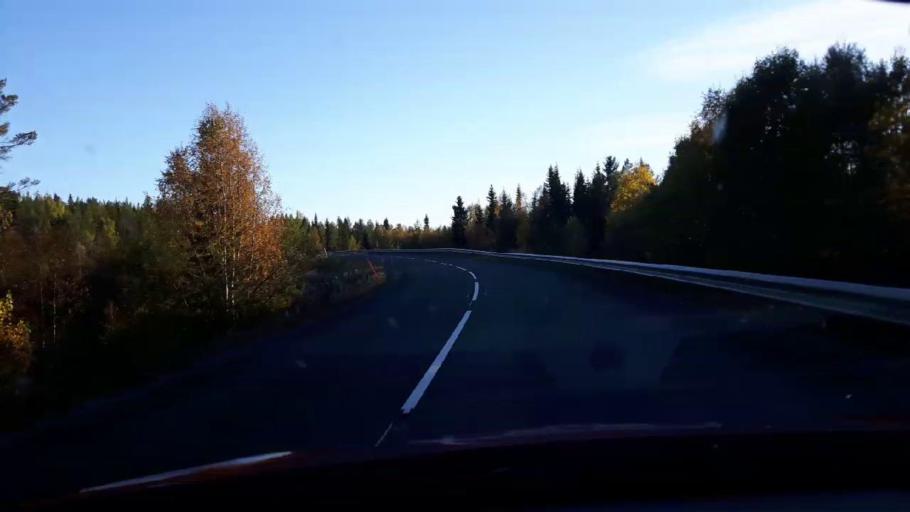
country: SE
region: Jaemtland
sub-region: OEstersunds Kommun
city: Lit
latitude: 63.4572
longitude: 14.8456
